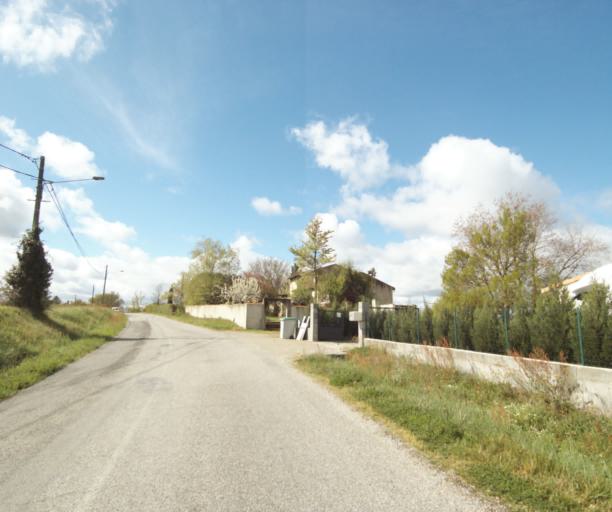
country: FR
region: Midi-Pyrenees
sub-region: Departement de l'Ariege
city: Saverdun
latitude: 43.2324
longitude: 1.5662
